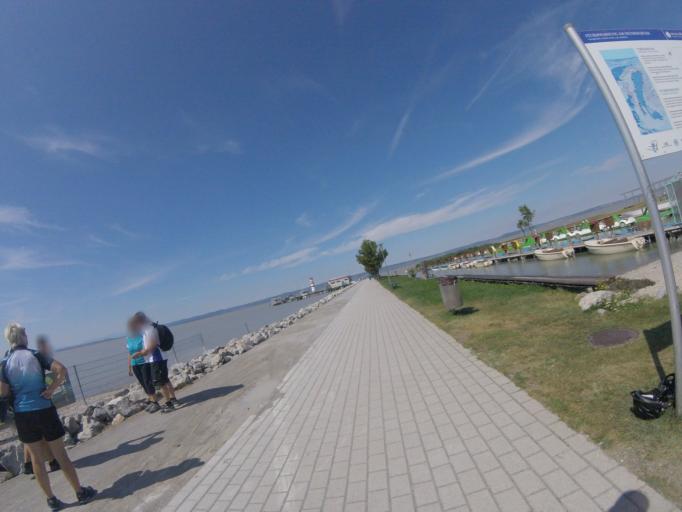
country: AT
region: Burgenland
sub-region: Politischer Bezirk Neusiedl am See
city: Podersdorf am See
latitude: 47.8595
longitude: 16.8292
